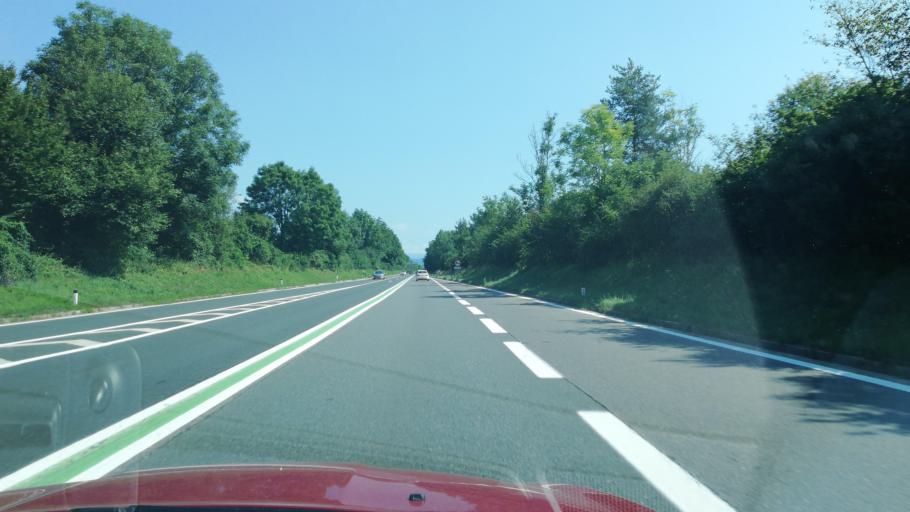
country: AT
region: Carinthia
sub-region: Politischer Bezirk Klagenfurt Land
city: Maria Saal
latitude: 46.6708
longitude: 14.3215
